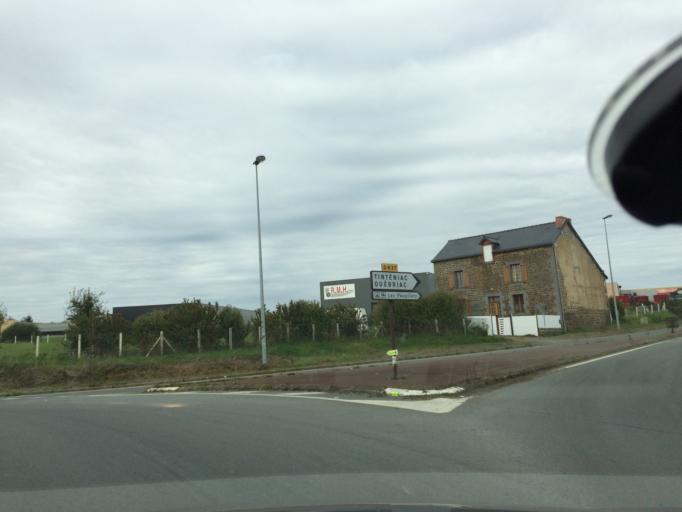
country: FR
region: Brittany
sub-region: Departement d'Ille-et-Vilaine
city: Hede-Bazouges
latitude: 48.3005
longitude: -1.8144
